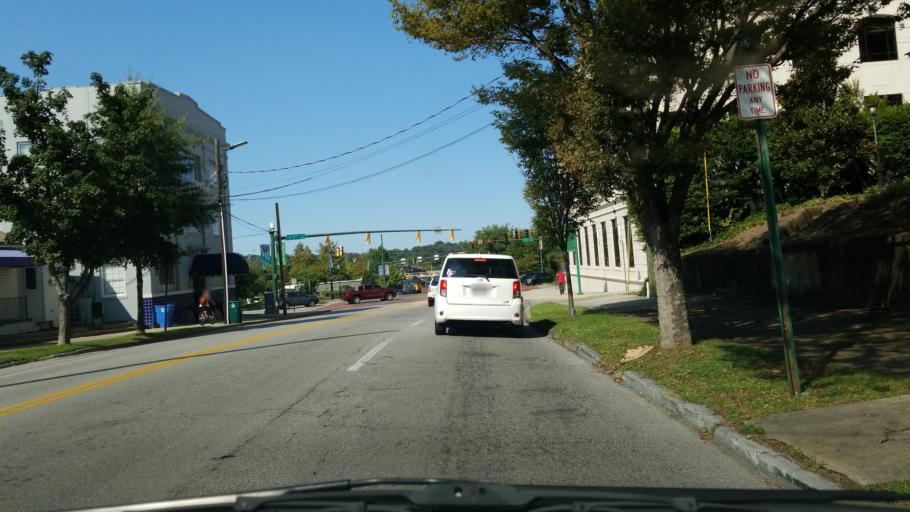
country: US
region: Tennessee
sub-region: Hamilton County
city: Chattanooga
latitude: 35.0516
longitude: -85.3050
